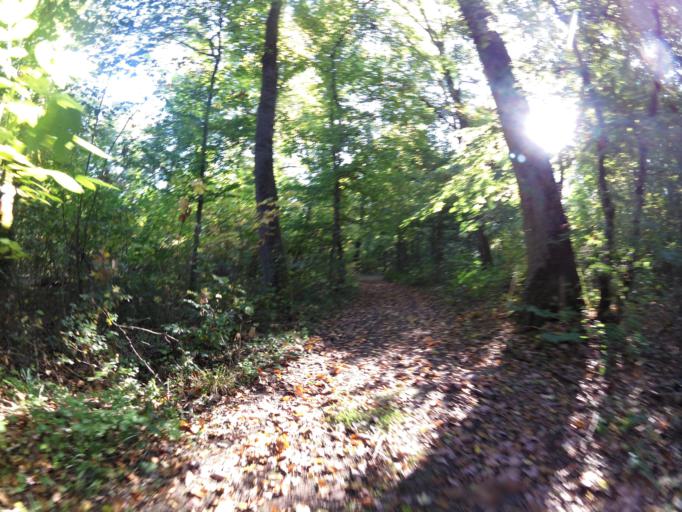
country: DE
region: Bavaria
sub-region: Regierungsbezirk Unterfranken
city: Ochsenfurt
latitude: 49.6828
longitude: 10.0454
